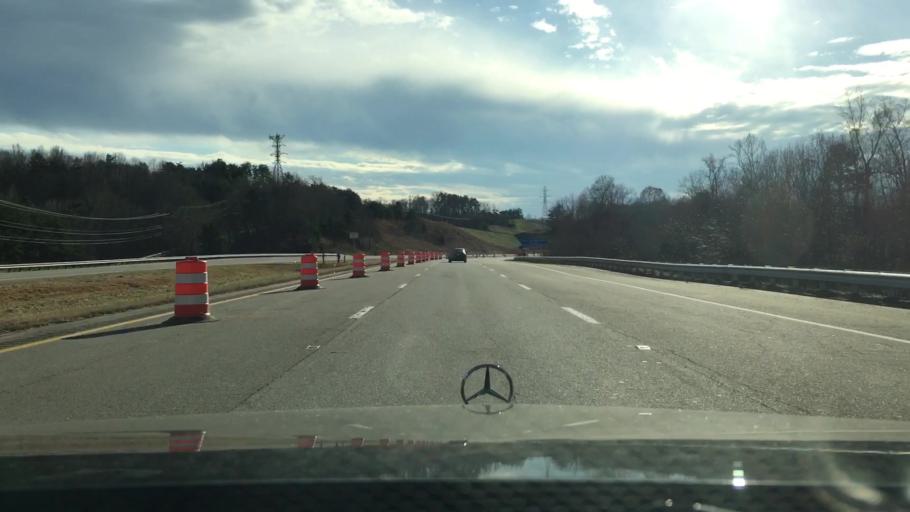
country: US
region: Virginia
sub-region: City of Danville
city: Danville
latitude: 36.5794
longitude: -79.3613
